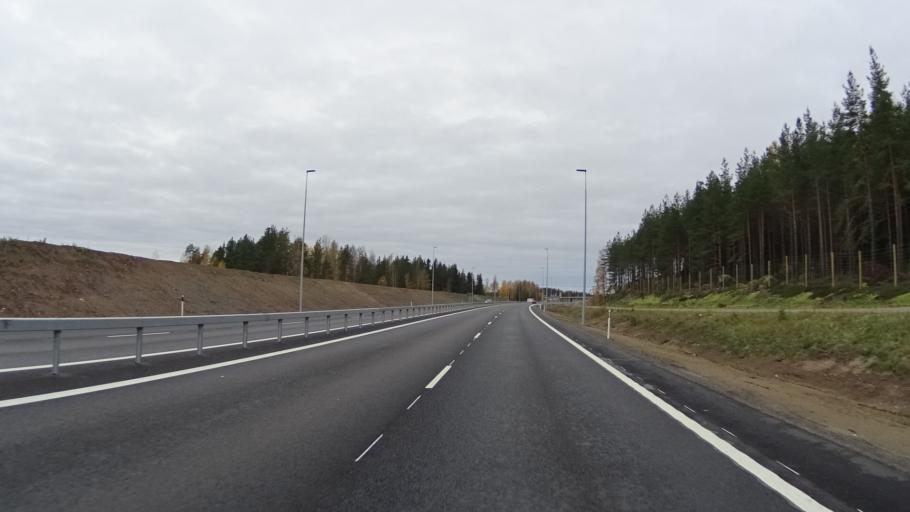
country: FI
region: South Karelia
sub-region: Lappeenranta
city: Luumaeki
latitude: 60.9308
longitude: 27.6445
